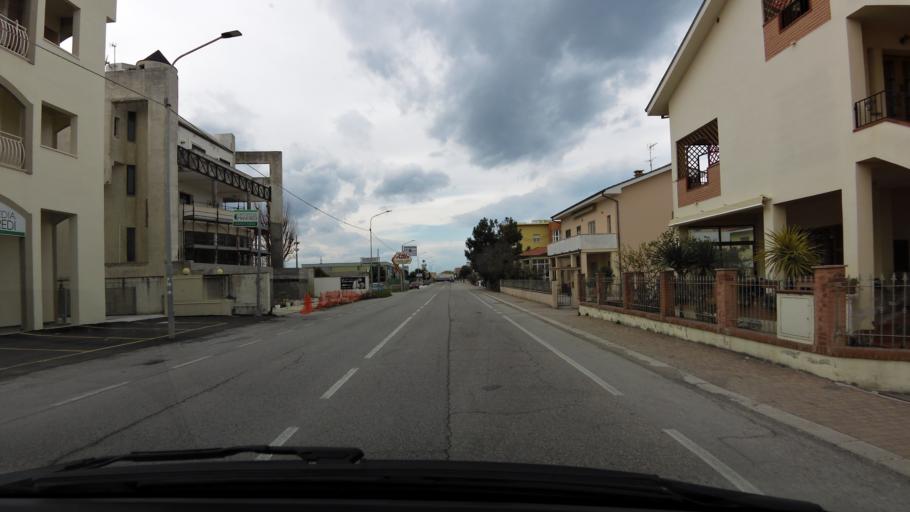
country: IT
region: The Marches
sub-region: Provincia di Ancona
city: Senigallia
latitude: 43.7364
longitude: 13.1896
